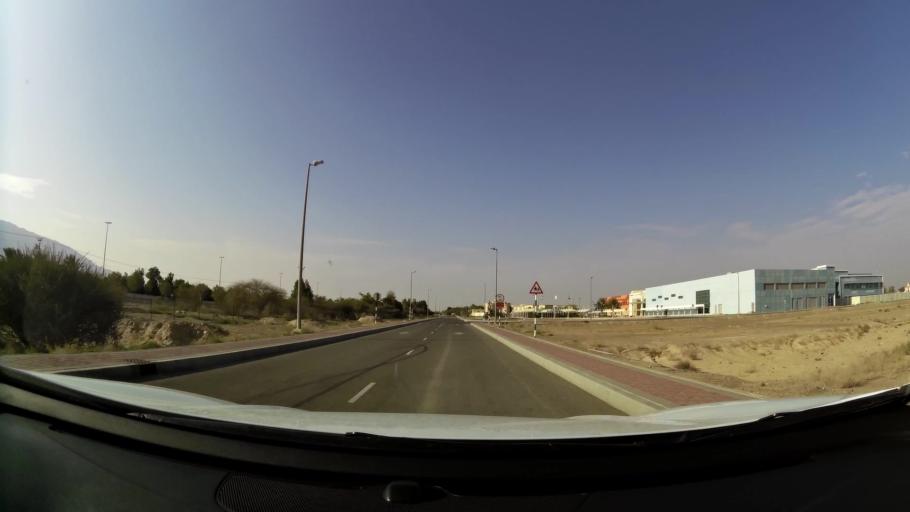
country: AE
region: Abu Dhabi
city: Al Ain
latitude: 24.0473
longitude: 55.8431
